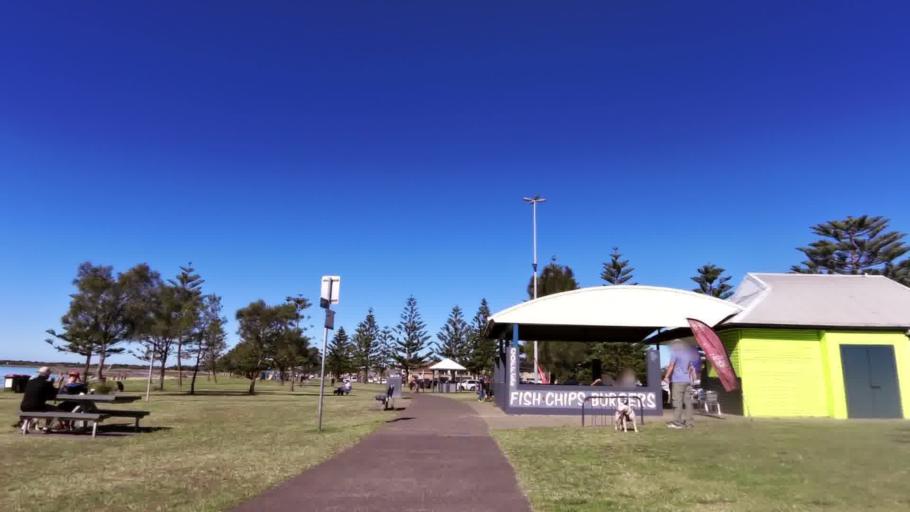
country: AU
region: New South Wales
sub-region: Shellharbour
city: Lake Illawarra
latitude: -34.5394
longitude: 150.8663
